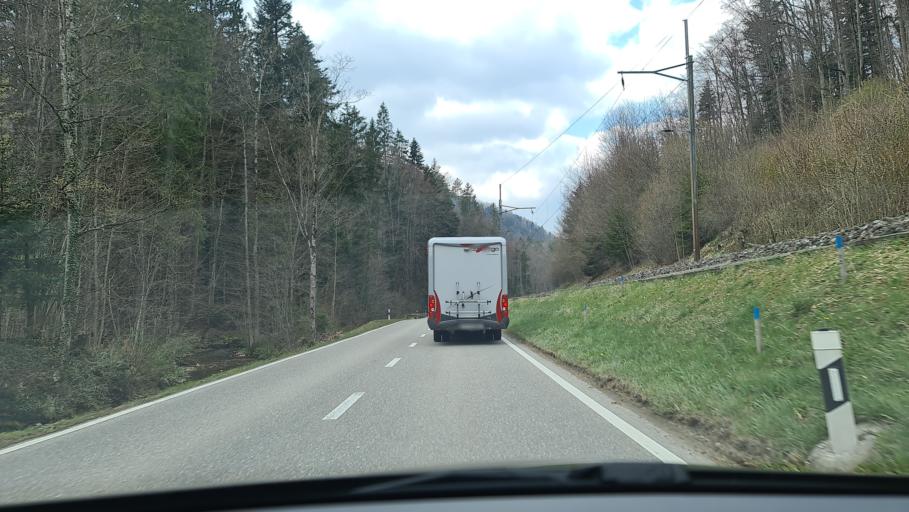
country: CH
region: Solothurn
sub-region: Bezirk Lebern
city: Selzach
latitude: 47.2739
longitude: 7.4534
